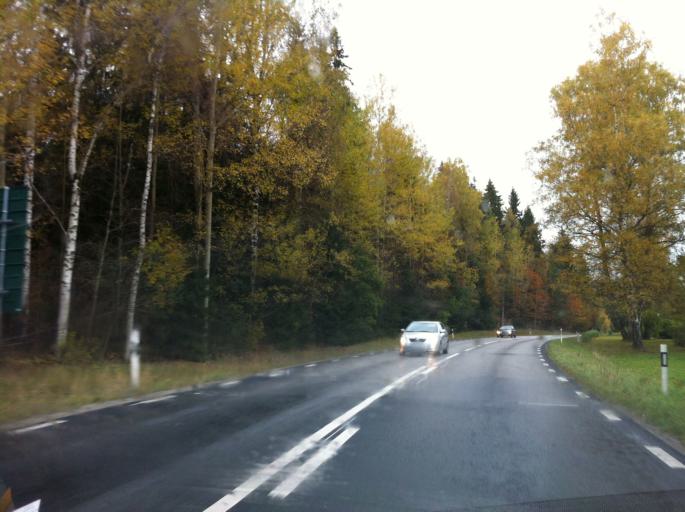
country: SE
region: OErebro
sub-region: Lindesbergs Kommun
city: Stora
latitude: 59.6642
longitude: 15.0988
